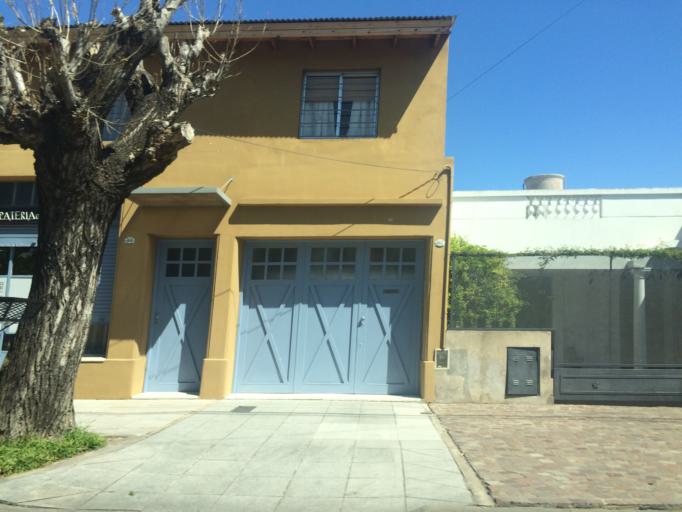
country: AR
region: Buenos Aires
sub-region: Partido de Lanus
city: Lanus
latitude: -34.7183
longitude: -58.3983
